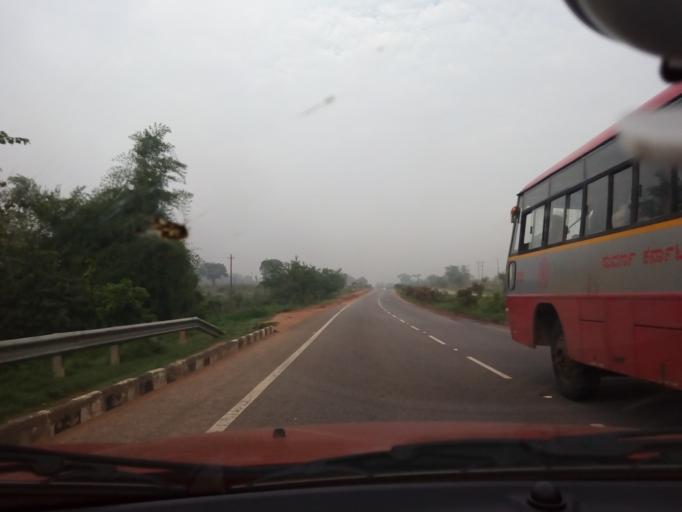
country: IN
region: Karnataka
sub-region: Ramanagara
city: Magadi
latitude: 13.0622
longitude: 77.1684
